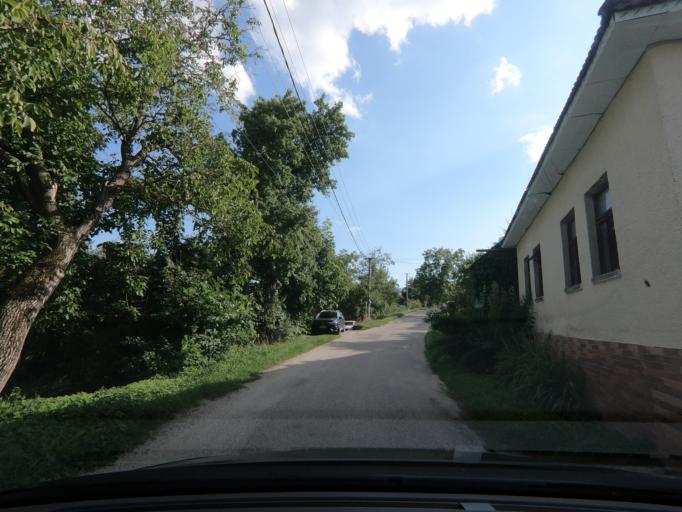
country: SK
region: Nitriansky
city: Stara Tura
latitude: 48.7580
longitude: 17.6820
